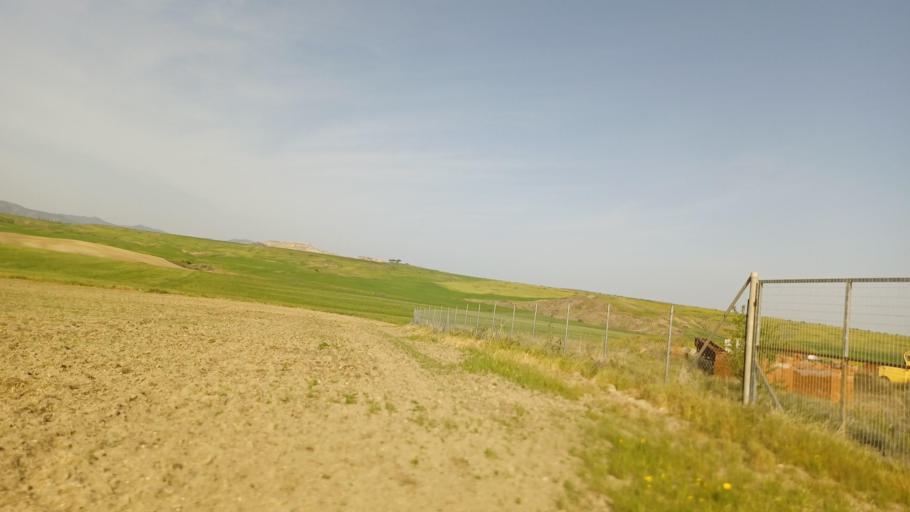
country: CY
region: Lefkosia
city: Lefka
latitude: 35.0931
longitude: 32.9441
